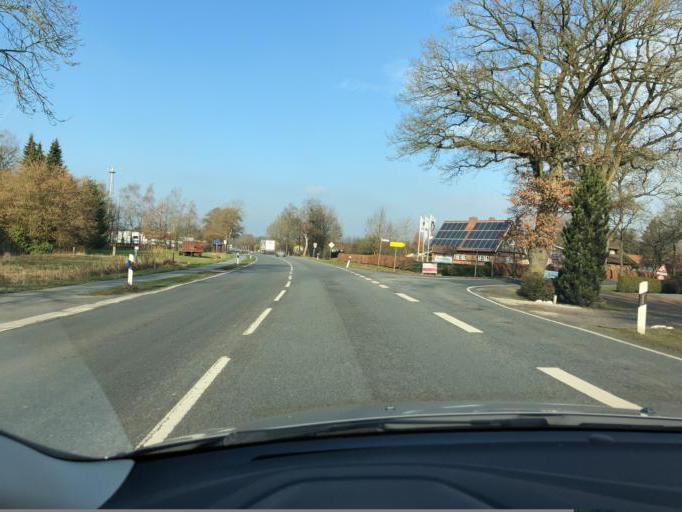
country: DE
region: Lower Saxony
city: Westerstede
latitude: 53.2852
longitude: 7.8969
